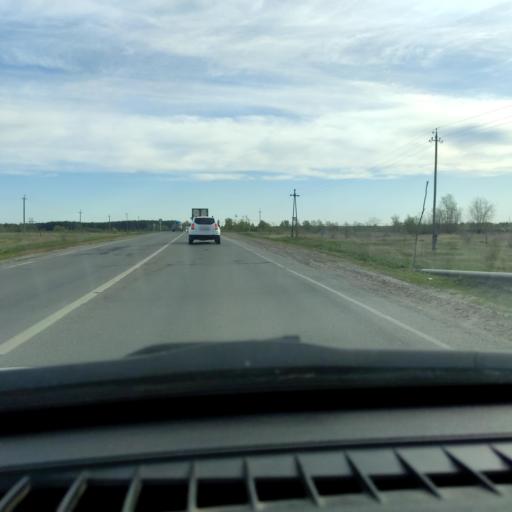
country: RU
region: Samara
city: Mirnyy
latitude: 53.5004
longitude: 50.2952
